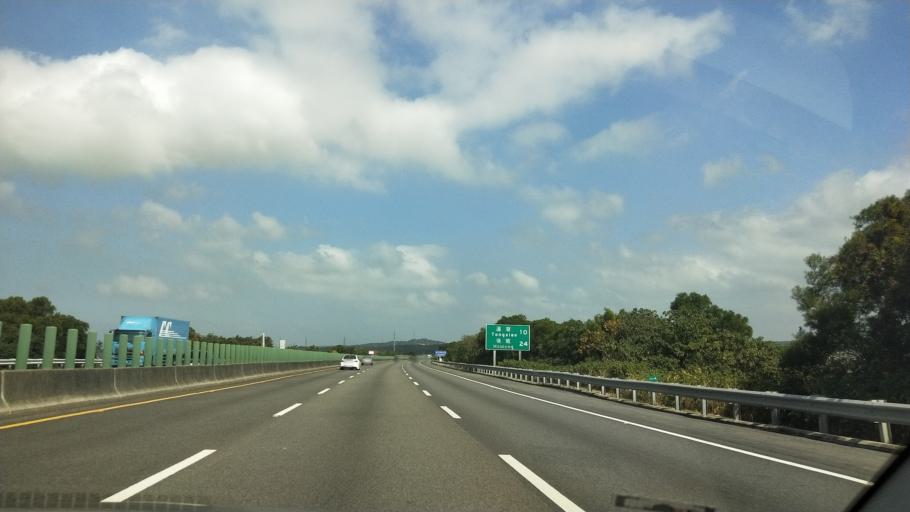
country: TW
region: Taiwan
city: Fengyuan
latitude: 24.4083
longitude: 120.6723
